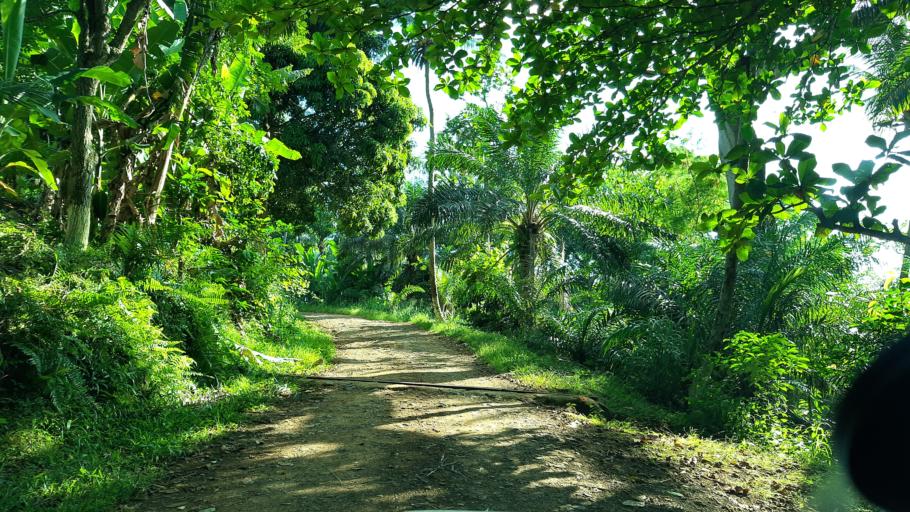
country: ST
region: Sao Tome Island
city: Sao Tome
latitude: 0.2455
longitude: 6.7383
